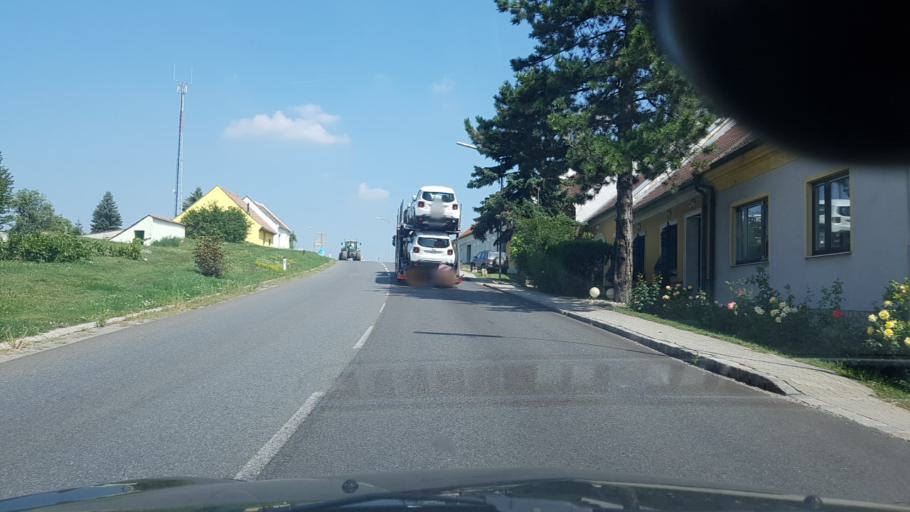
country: AT
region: Lower Austria
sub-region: Politischer Bezirk Mistelbach
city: Drasenhofen
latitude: 48.7587
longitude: 16.6474
